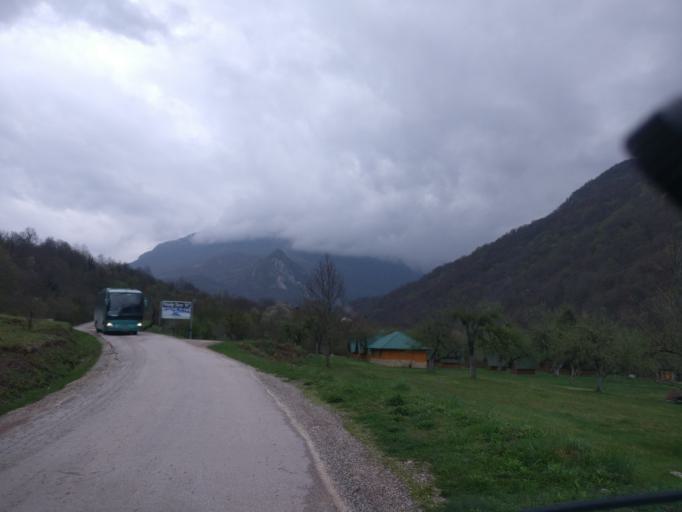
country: BA
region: Republika Srpska
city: Foca
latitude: 43.3534
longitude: 18.8236
